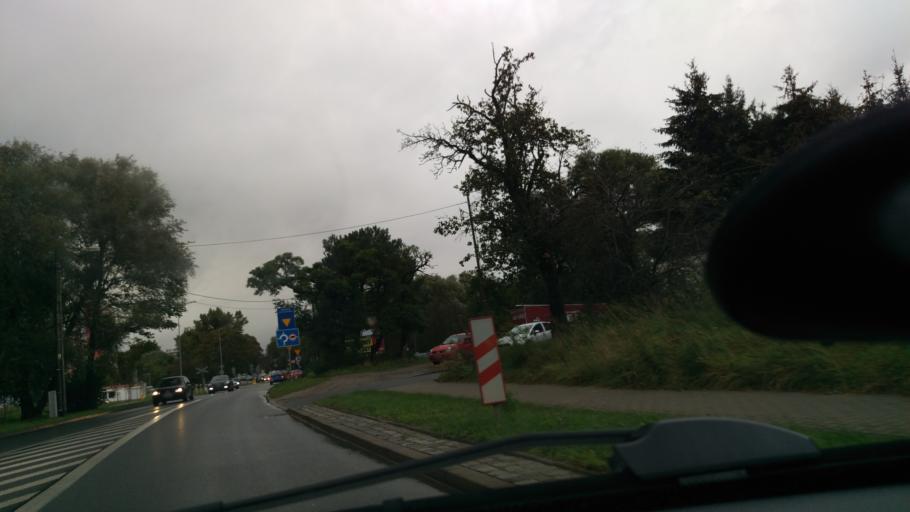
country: PL
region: West Pomeranian Voivodeship
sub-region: Szczecin
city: Szczecin
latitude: 53.3724
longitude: 14.6608
